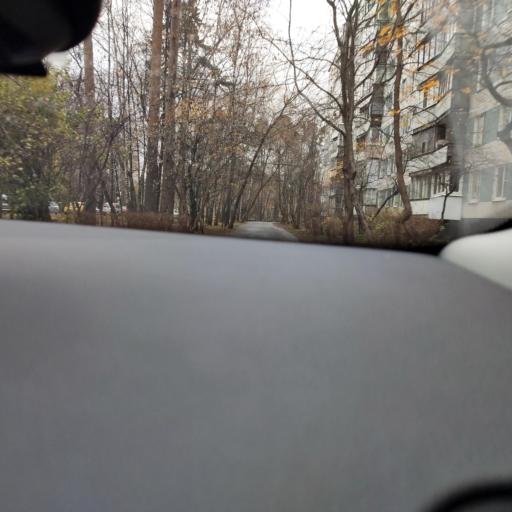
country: RU
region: Moscow
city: Vatutino
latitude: 55.8860
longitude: 37.6966
